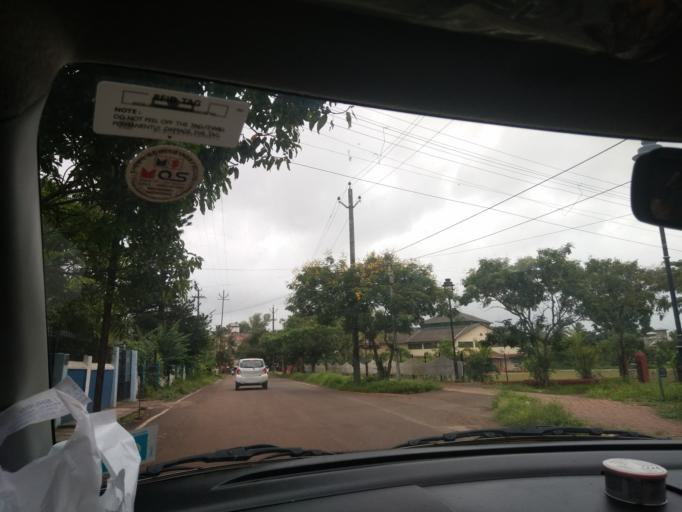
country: IN
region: Goa
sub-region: North Goa
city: Serula
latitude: 15.5329
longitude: 73.8252
